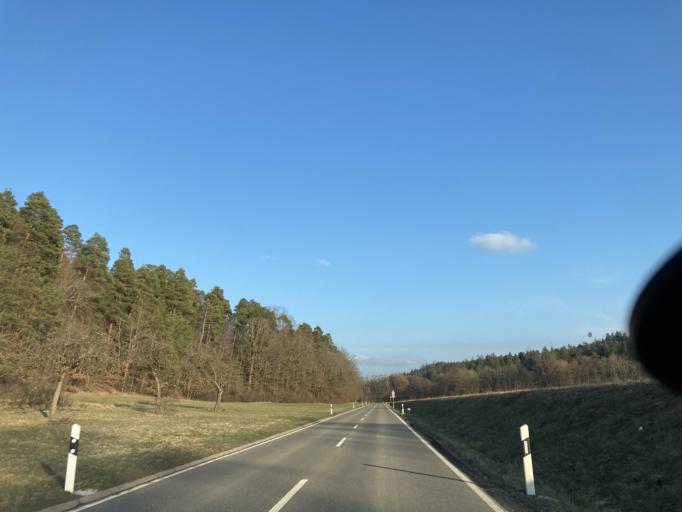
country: DE
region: Baden-Wuerttemberg
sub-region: Tuebingen Region
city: Rottenburg
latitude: 48.4320
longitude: 8.9502
